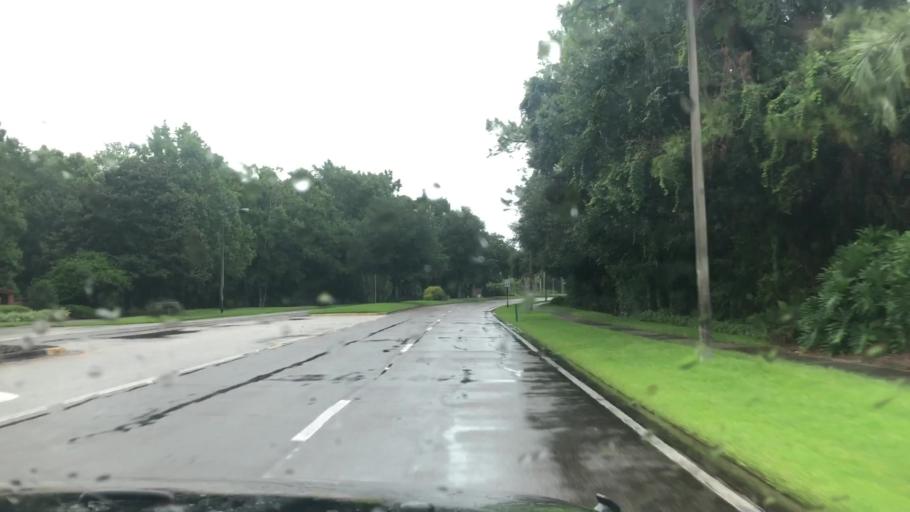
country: US
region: Florida
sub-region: Hillsborough County
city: University
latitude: 28.1021
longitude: -82.4019
